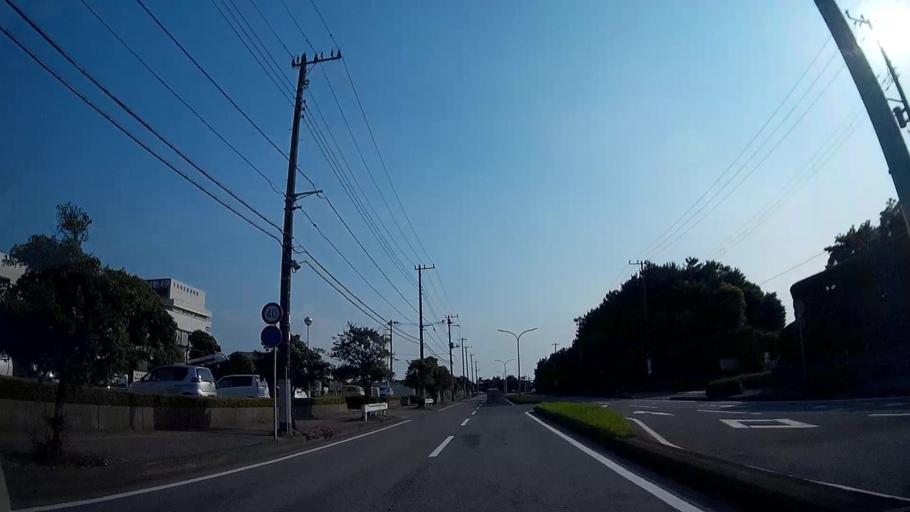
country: JP
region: Chiba
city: Chiba
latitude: 35.6296
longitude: 140.0516
